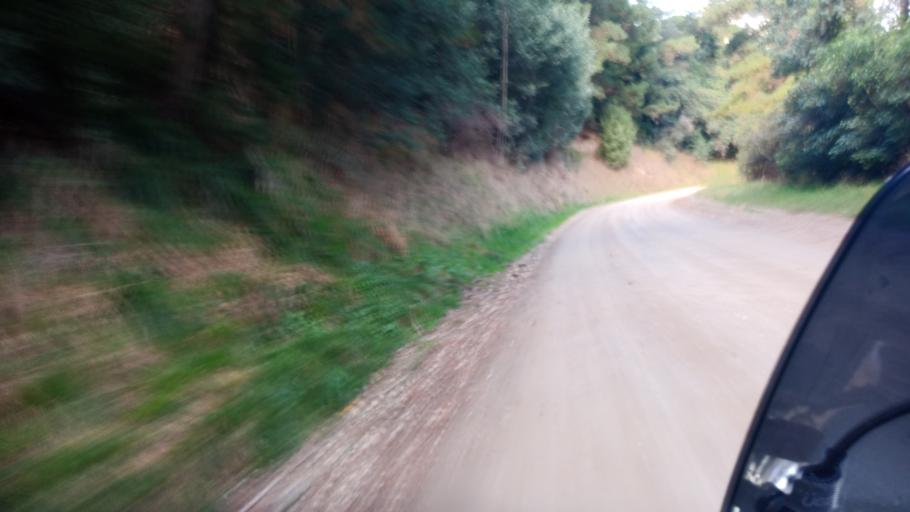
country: NZ
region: Gisborne
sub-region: Gisborne District
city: Gisborne
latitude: -38.5358
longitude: 177.5245
